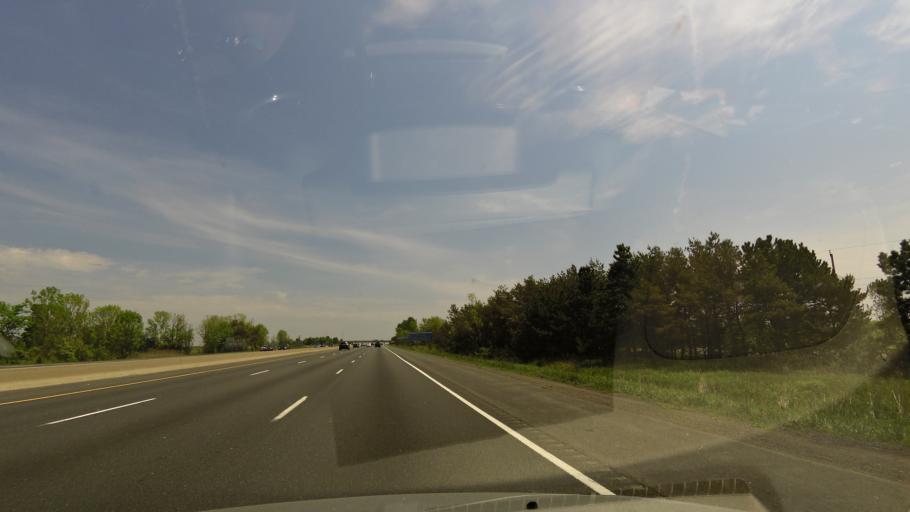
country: CA
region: Ontario
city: Oshawa
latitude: 43.9008
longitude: -78.6520
